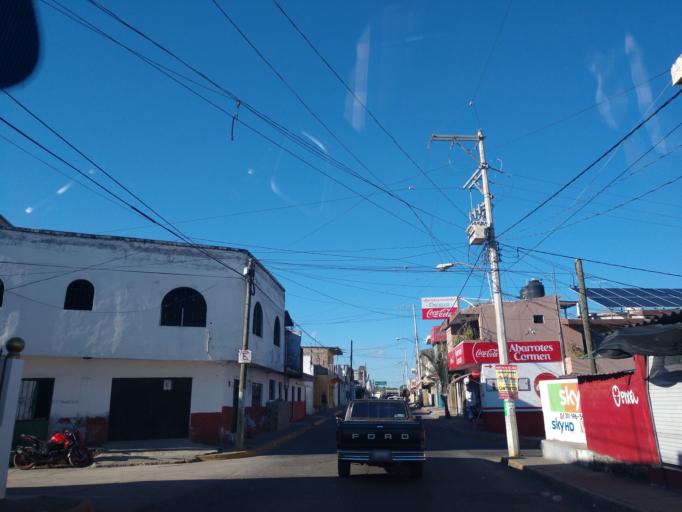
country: MX
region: Nayarit
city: Xalisco
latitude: 21.4498
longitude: -104.8979
